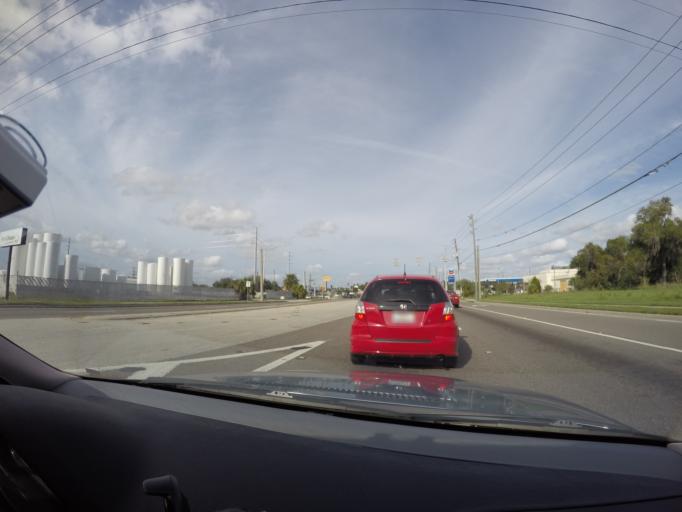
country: US
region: Florida
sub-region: Orange County
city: Belle Isle
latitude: 28.4497
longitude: -81.3637
